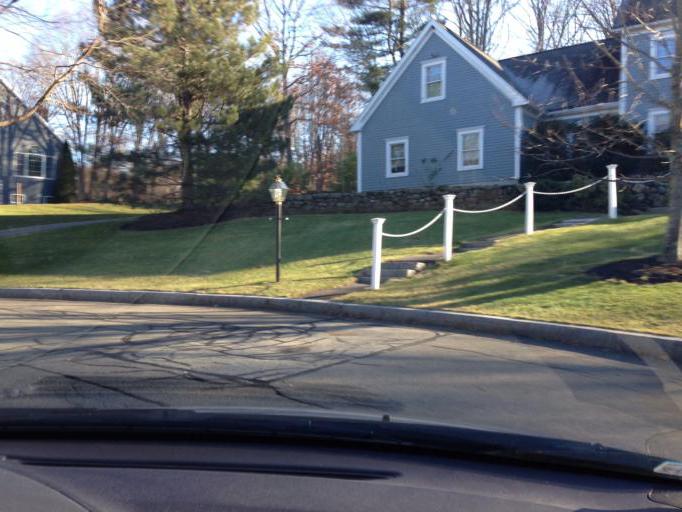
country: US
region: Massachusetts
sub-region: Middlesex County
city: Bedford
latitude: 42.5167
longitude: -71.2751
